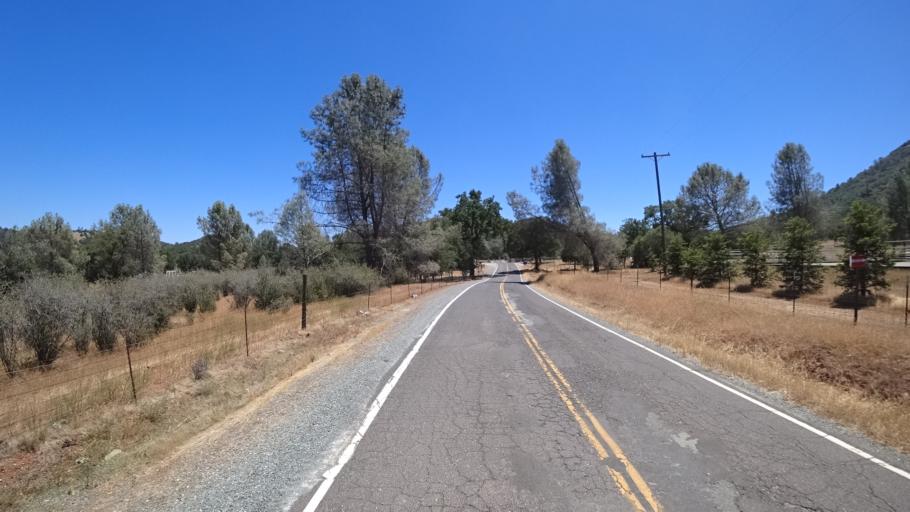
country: US
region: California
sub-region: Calaveras County
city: Copperopolis
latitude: 38.0661
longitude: -120.6570
